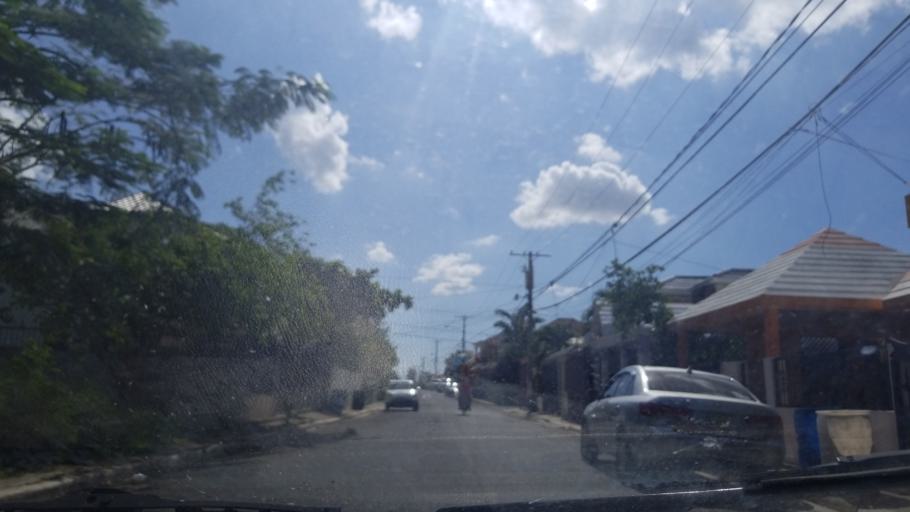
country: DO
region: Santiago
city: Santiago de los Caballeros
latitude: 19.4856
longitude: -70.6887
